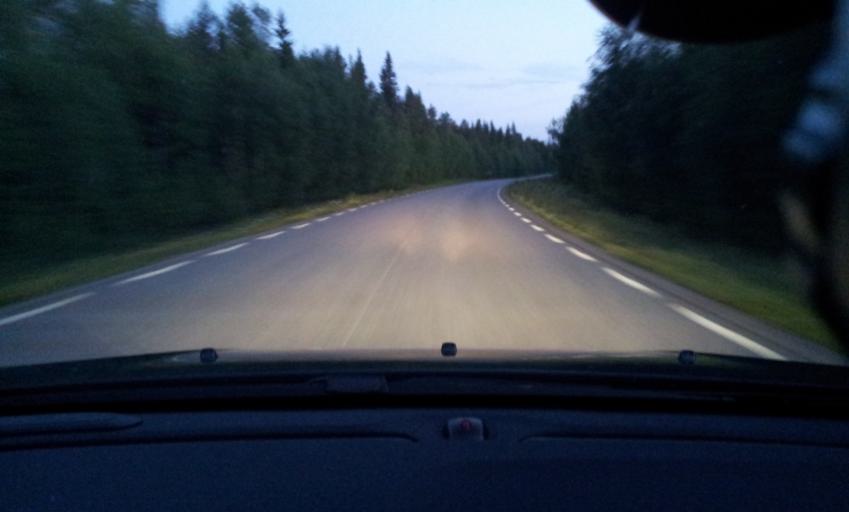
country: SE
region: Jaemtland
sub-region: Braecke Kommun
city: Braecke
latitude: 62.7373
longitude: 15.1910
